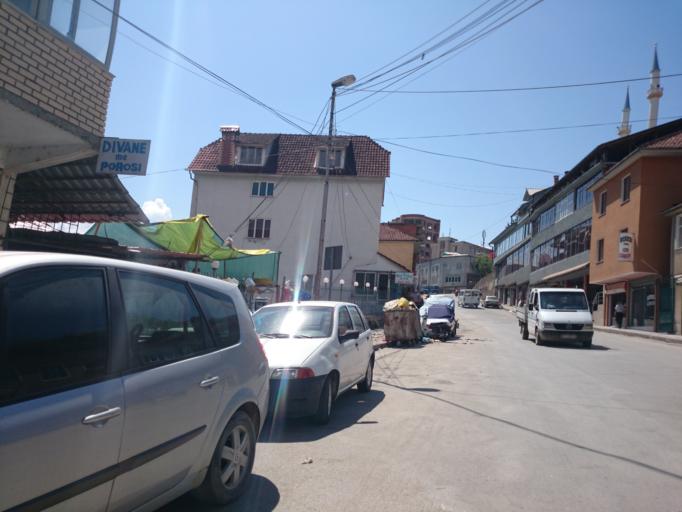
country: AL
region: Diber
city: Peshkopi
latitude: 41.6844
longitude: 20.4338
